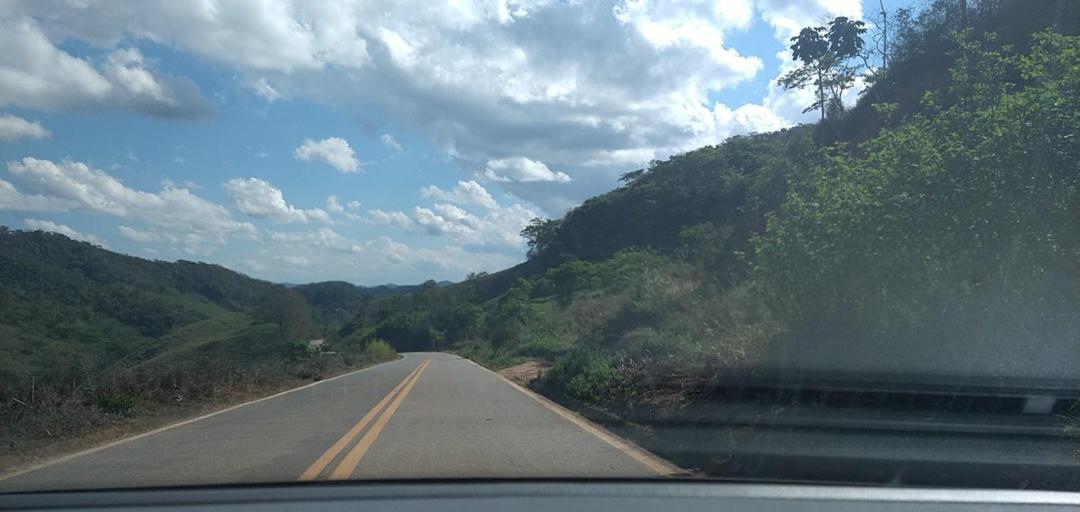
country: BR
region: Minas Gerais
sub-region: Alvinopolis
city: Alvinopolis
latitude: -20.0467
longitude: -43.0352
